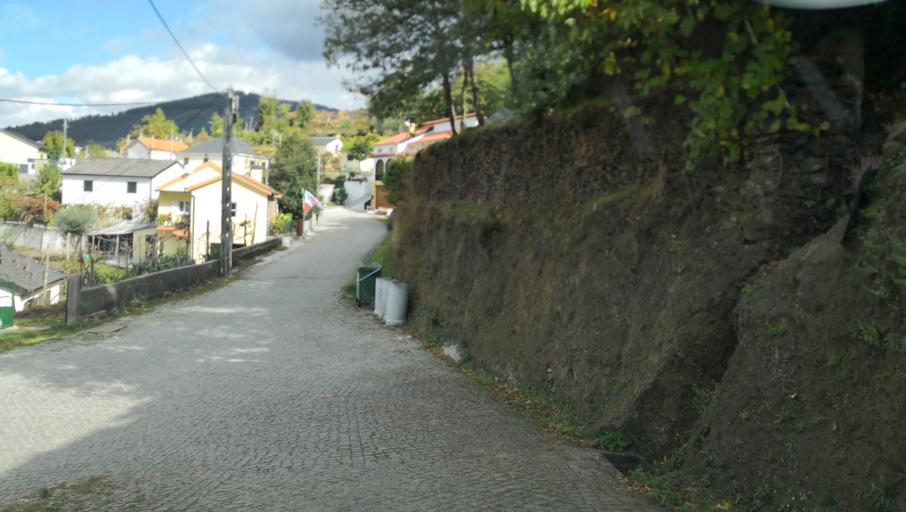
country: PT
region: Vila Real
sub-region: Mondim de Basto
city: Mondim de Basto
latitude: 41.3633
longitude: -7.8869
